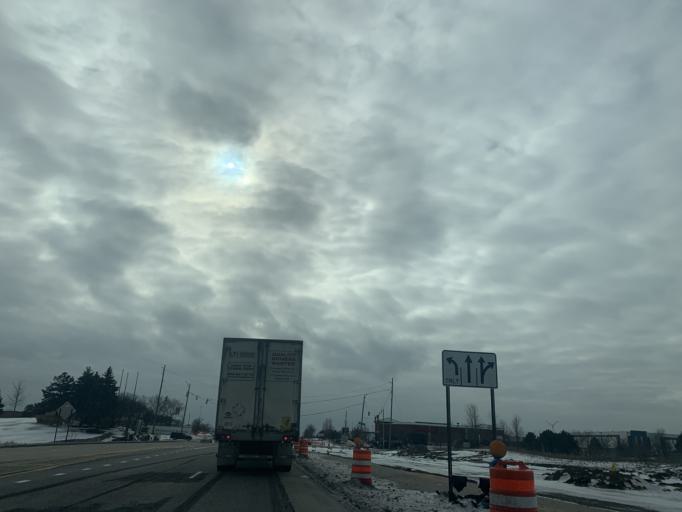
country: US
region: Illinois
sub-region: Will County
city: Romeoville
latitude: 41.6637
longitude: -88.1251
